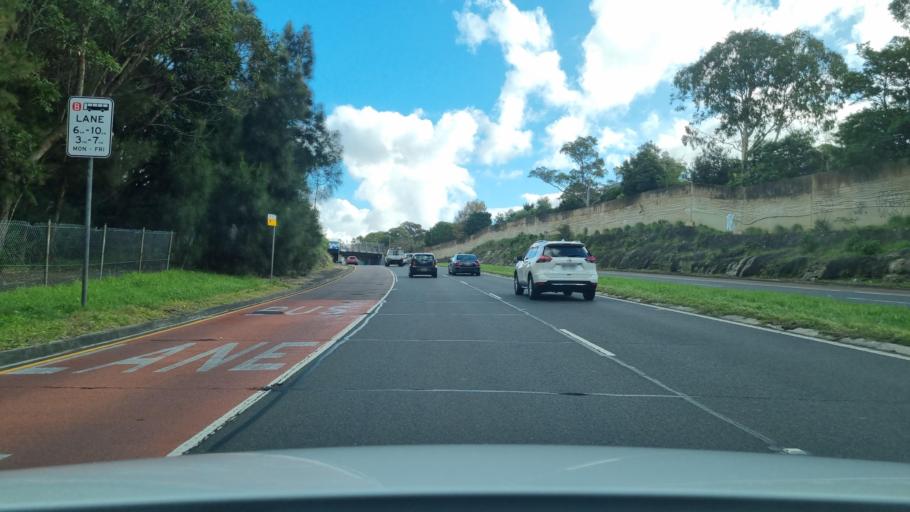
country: AU
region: New South Wales
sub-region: Manly Vale
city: Balgowlah
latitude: -33.7886
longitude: 151.2591
